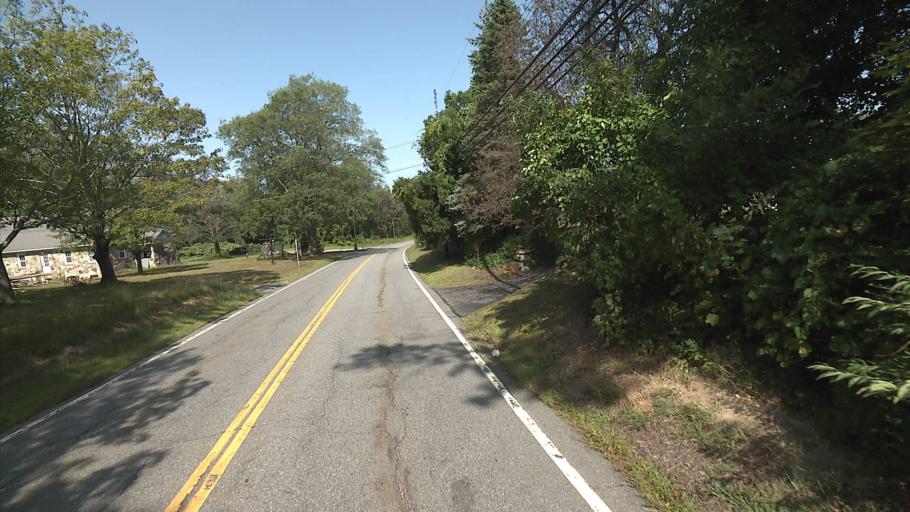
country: US
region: Connecticut
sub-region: Windham County
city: South Woodstock
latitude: 41.9519
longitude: -71.9796
